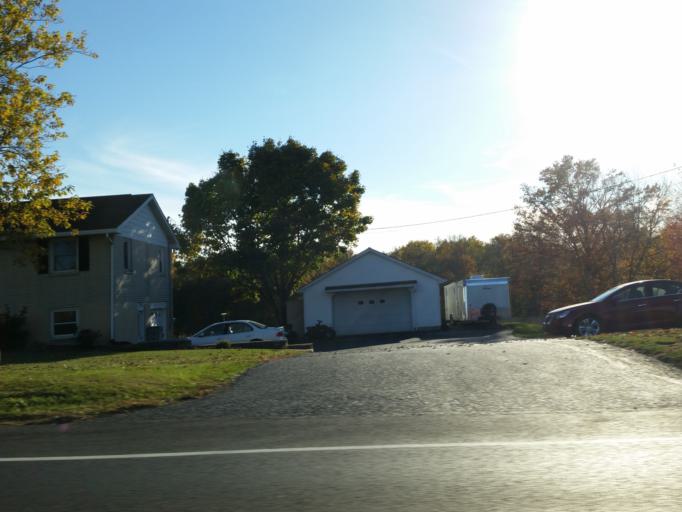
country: US
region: Pennsylvania
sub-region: Lebanon County
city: Annville
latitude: 40.3924
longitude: -76.5658
